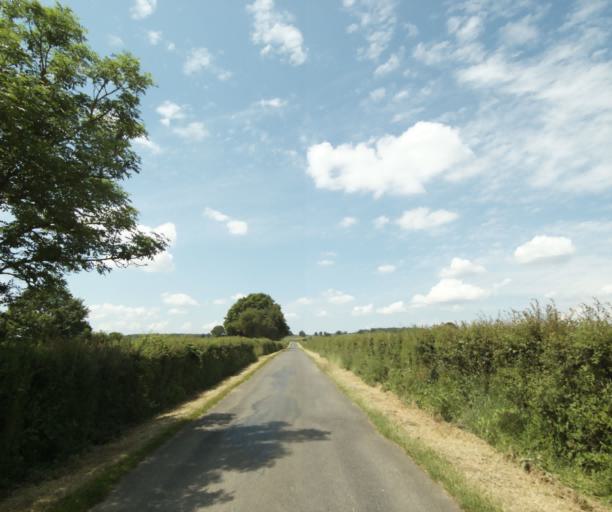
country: FR
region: Bourgogne
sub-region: Departement de Saone-et-Loire
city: Perrecy-les-Forges
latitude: 46.5807
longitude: 4.1492
